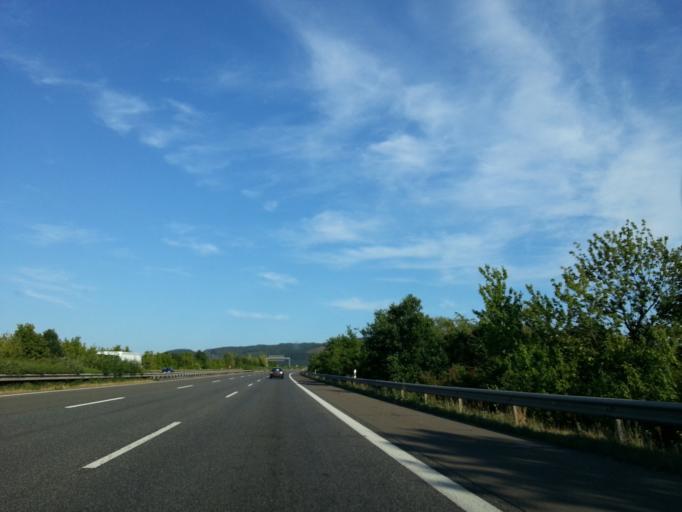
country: DE
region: Rheinland-Pfalz
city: Longuich
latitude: 49.7995
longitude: 6.7675
